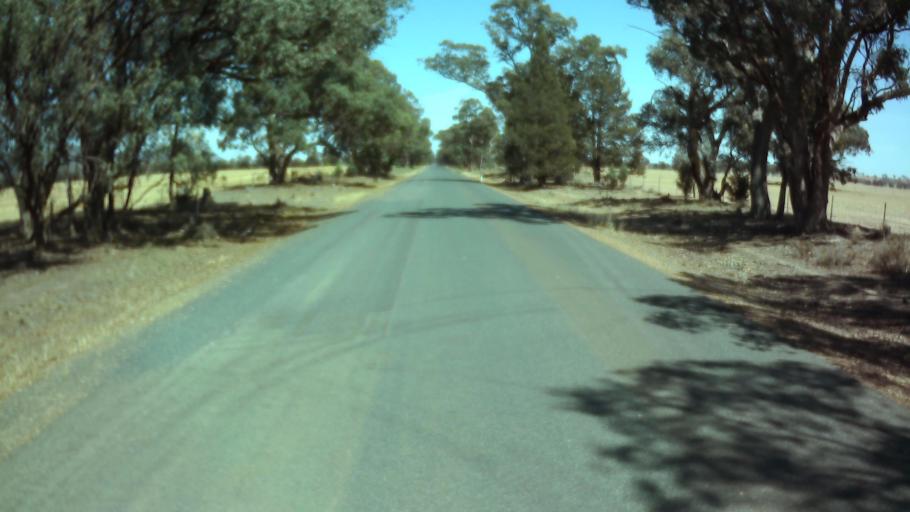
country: AU
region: New South Wales
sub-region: Weddin
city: Grenfell
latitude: -33.8682
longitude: 148.0700
